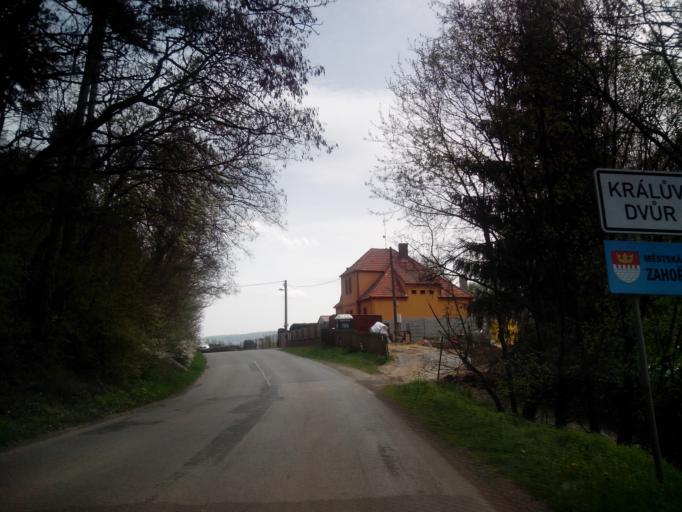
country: CZ
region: Central Bohemia
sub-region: Okres Beroun
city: Kraluv Dvur
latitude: 49.9554
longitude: 14.0132
